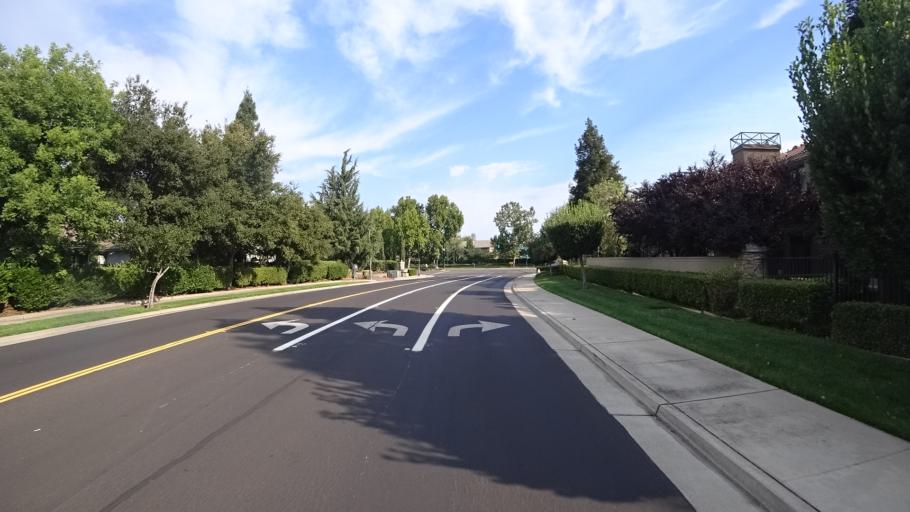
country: US
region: California
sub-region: Sacramento County
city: Laguna
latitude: 38.4032
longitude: -121.4673
